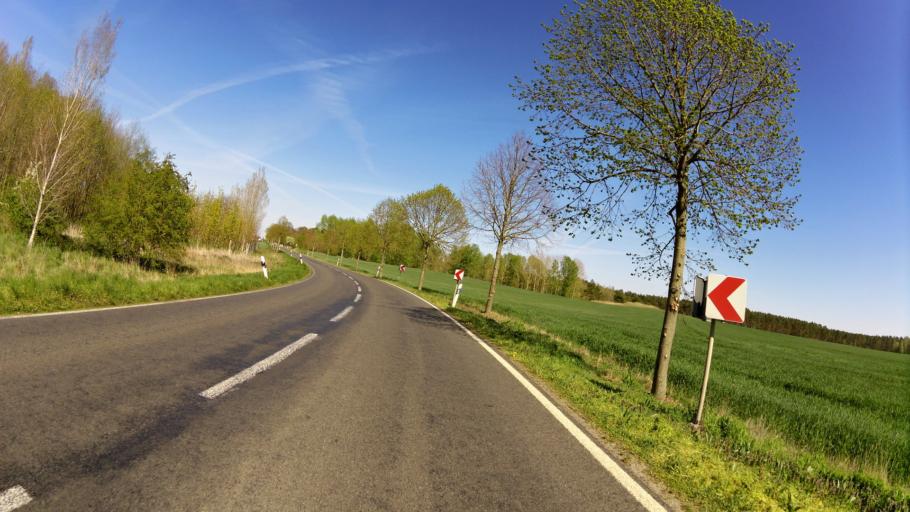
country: DE
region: Saxony-Anhalt
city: Kalbe
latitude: 52.6470
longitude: 11.4542
